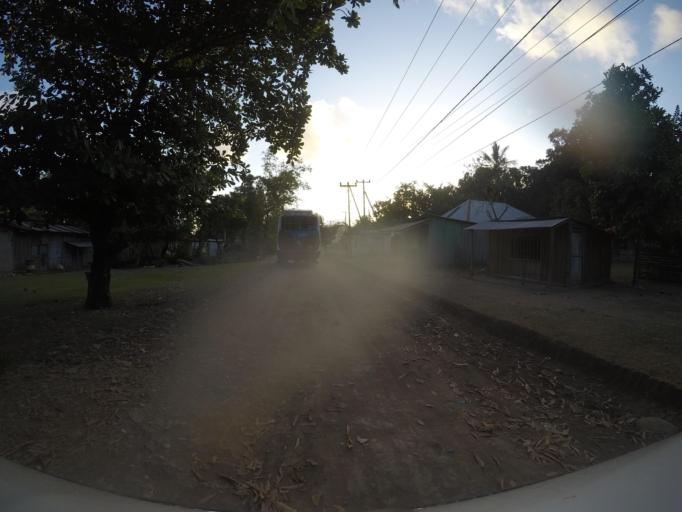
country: TL
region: Baucau
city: Venilale
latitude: -8.7489
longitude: 126.7046
